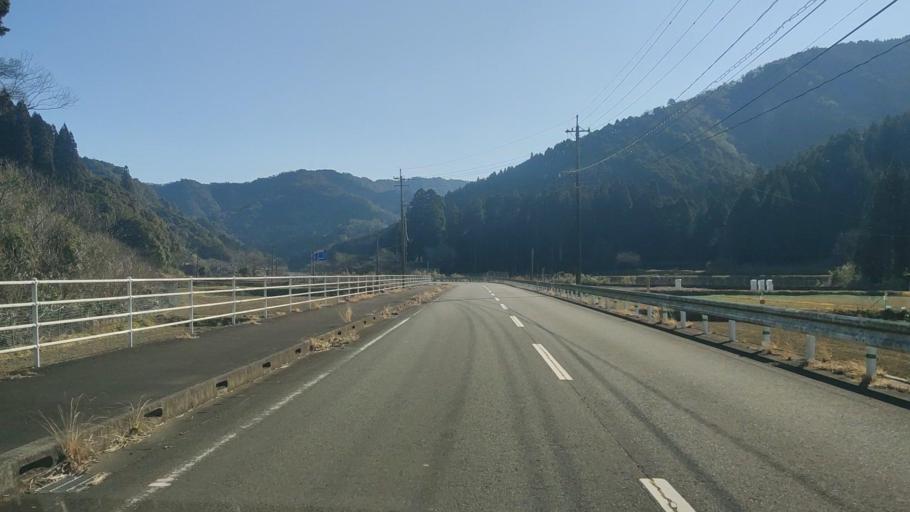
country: JP
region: Oita
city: Saiki
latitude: 32.7748
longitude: 131.8243
